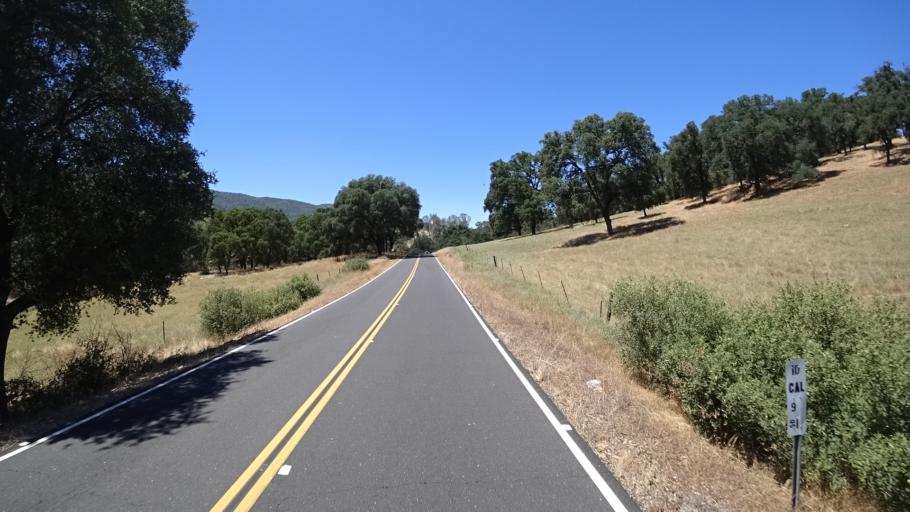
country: US
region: California
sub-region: Calaveras County
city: San Andreas
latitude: 38.1544
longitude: -120.6644
